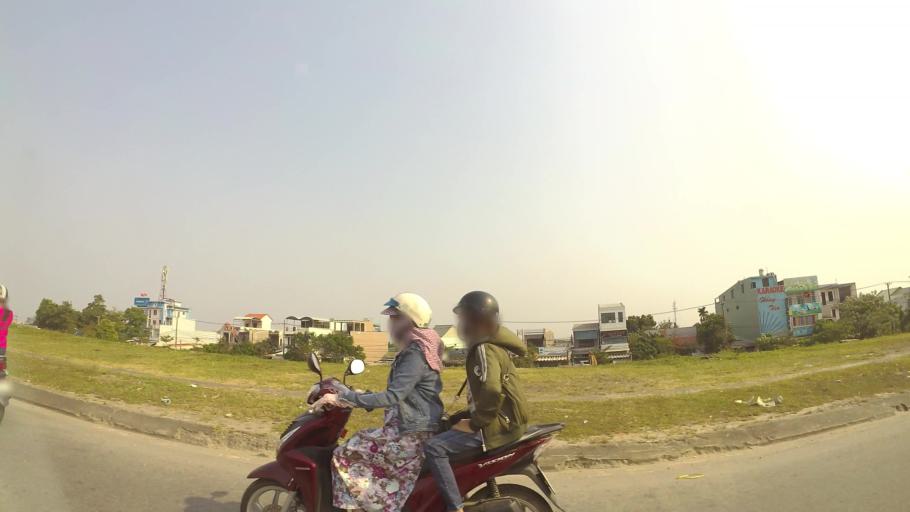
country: VN
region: Da Nang
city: Cam Le
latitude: 16.0135
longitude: 108.1897
